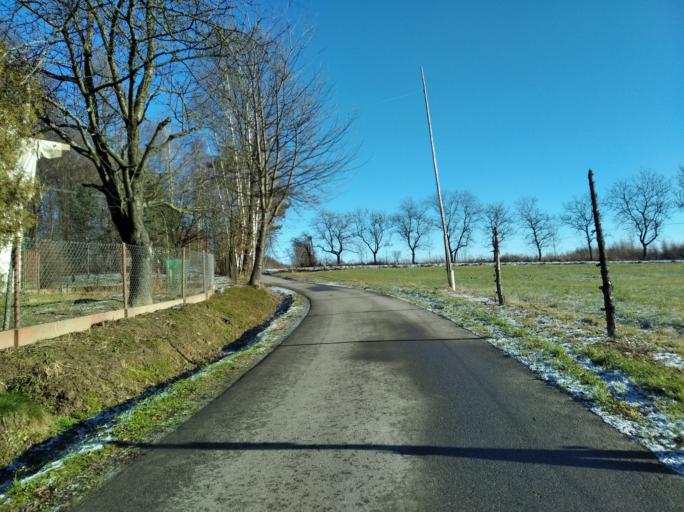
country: PL
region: Subcarpathian Voivodeship
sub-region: Powiat ropczycko-sedziszowski
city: Iwierzyce
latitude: 49.9680
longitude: 21.7418
